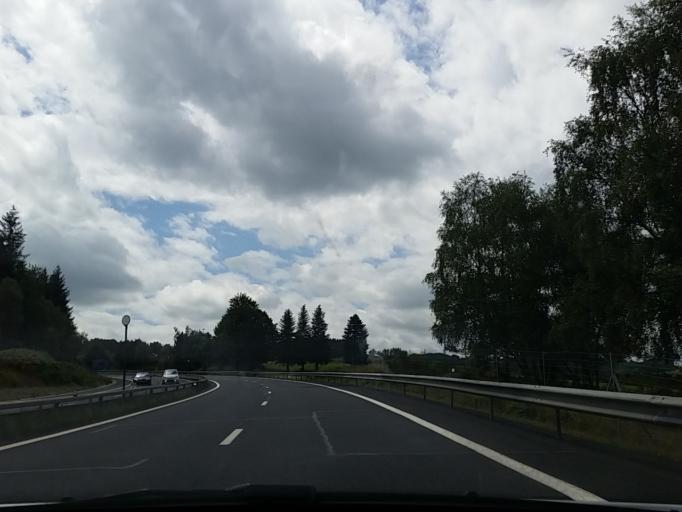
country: FR
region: Auvergne
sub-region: Departement du Cantal
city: Saint-Flour
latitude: 45.1328
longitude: 3.1373
